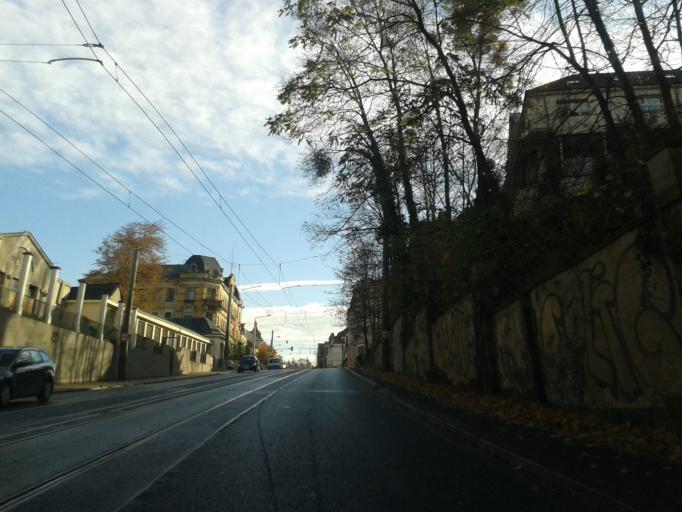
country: DE
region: Saxony
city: Albertstadt
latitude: 51.0644
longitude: 13.8188
